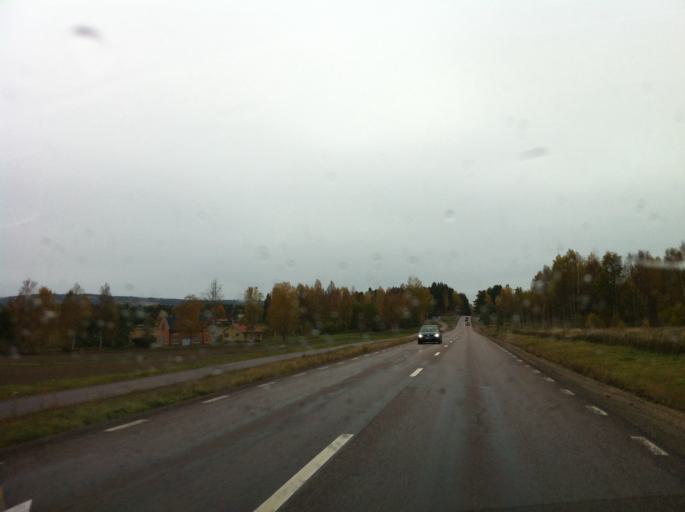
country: SE
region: Dalarna
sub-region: Ludvika Kommun
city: Grangesberg
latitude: 60.2558
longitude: 14.9813
